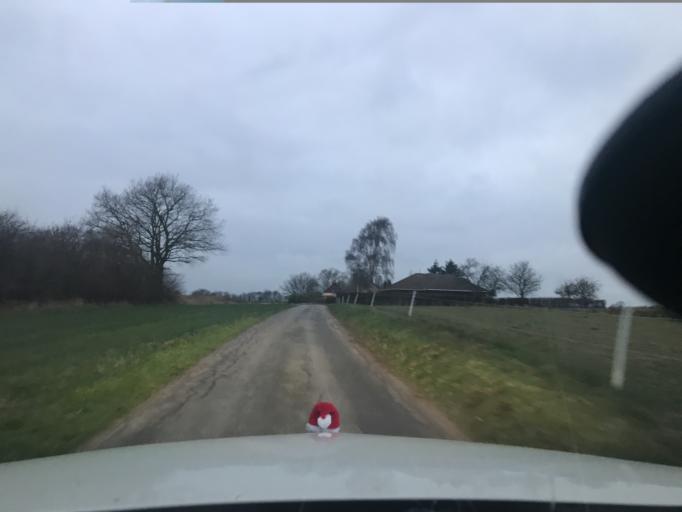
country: DK
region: South Denmark
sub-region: Sonderborg Kommune
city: Dybbol
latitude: 54.8474
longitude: 9.7430
